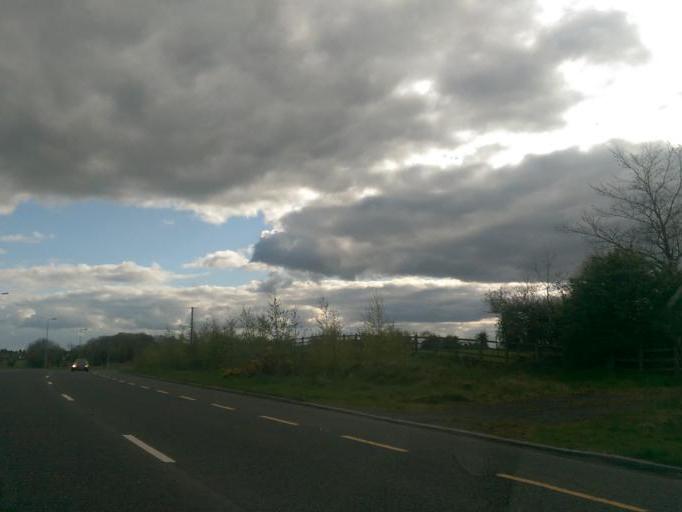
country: IE
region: Connaught
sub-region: County Galway
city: Ballinasloe
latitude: 53.3248
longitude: -8.1744
